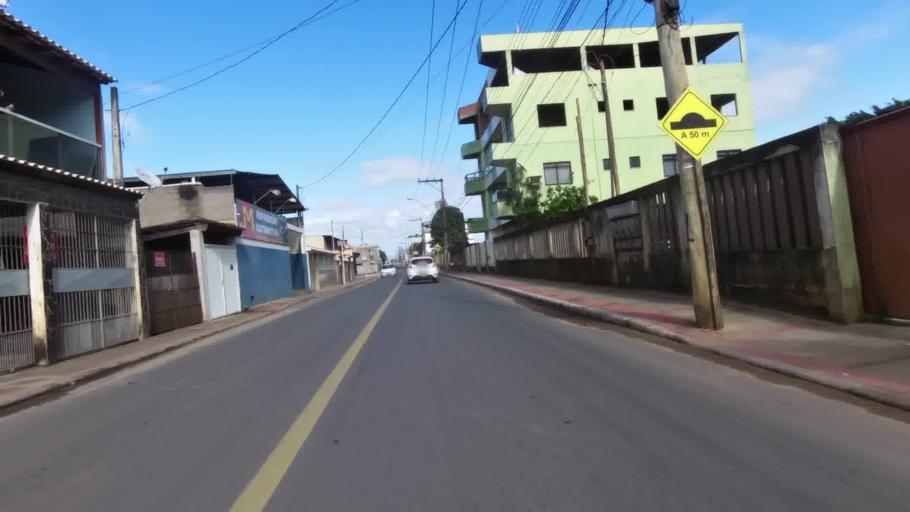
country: BR
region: Espirito Santo
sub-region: Piuma
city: Piuma
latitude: -20.8400
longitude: -40.7385
